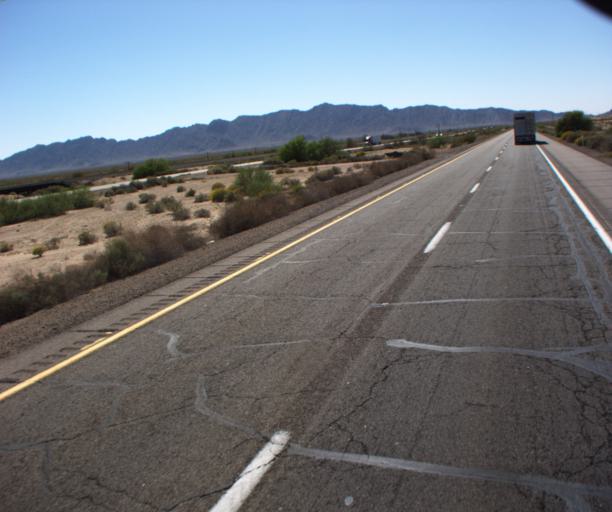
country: US
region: Arizona
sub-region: Yuma County
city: Wellton
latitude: 32.7511
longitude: -113.6615
